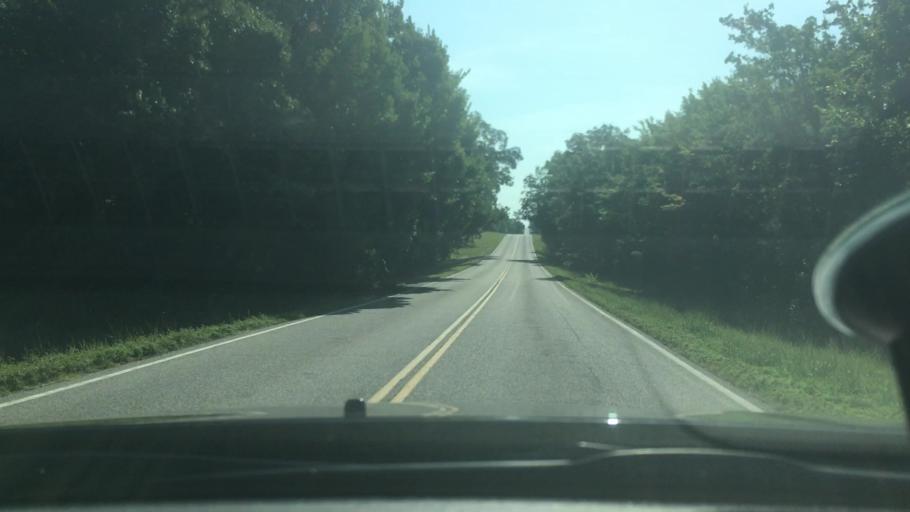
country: US
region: Oklahoma
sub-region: Garvin County
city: Pauls Valley
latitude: 34.6520
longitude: -97.3018
